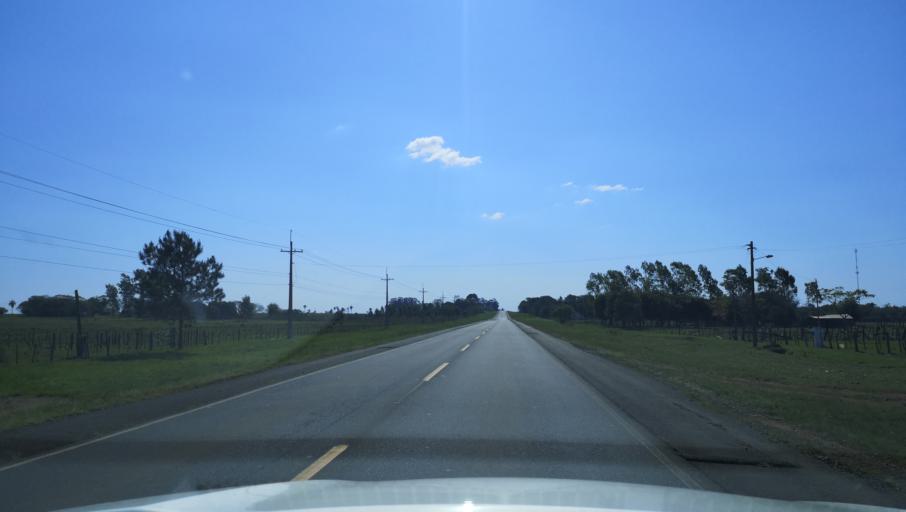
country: PY
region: Misiones
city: San Patricio
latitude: -27.0342
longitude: -56.6774
